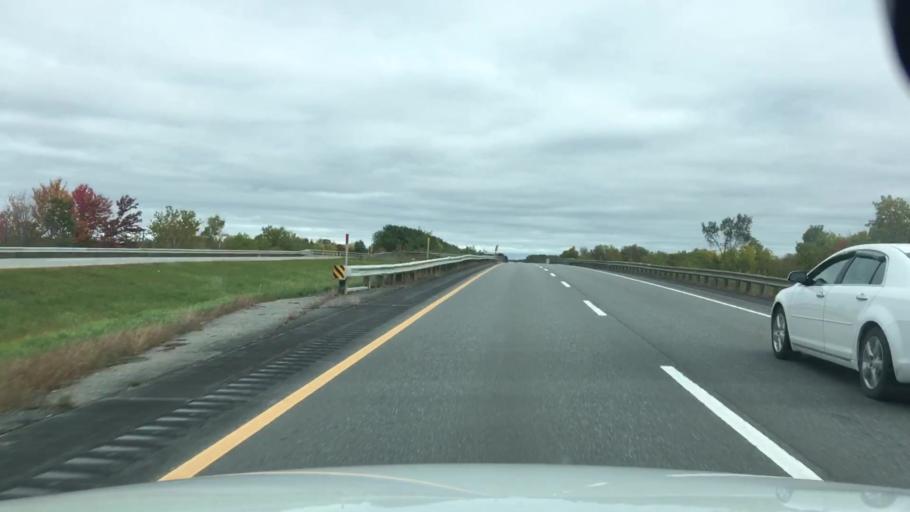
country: US
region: Maine
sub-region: Penobscot County
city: Newport
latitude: 44.8300
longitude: -69.2838
